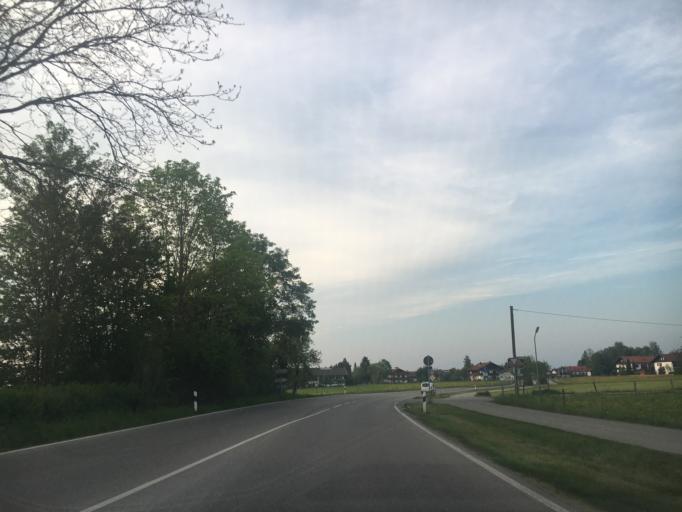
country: DE
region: Bavaria
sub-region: Upper Bavaria
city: Benediktbeuern
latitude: 47.6995
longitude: 11.4050
